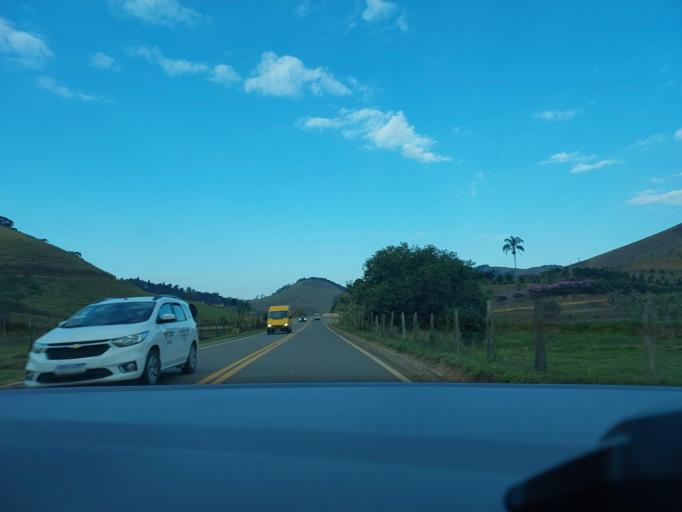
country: BR
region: Minas Gerais
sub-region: Muriae
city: Muriae
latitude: -21.0508
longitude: -42.5160
